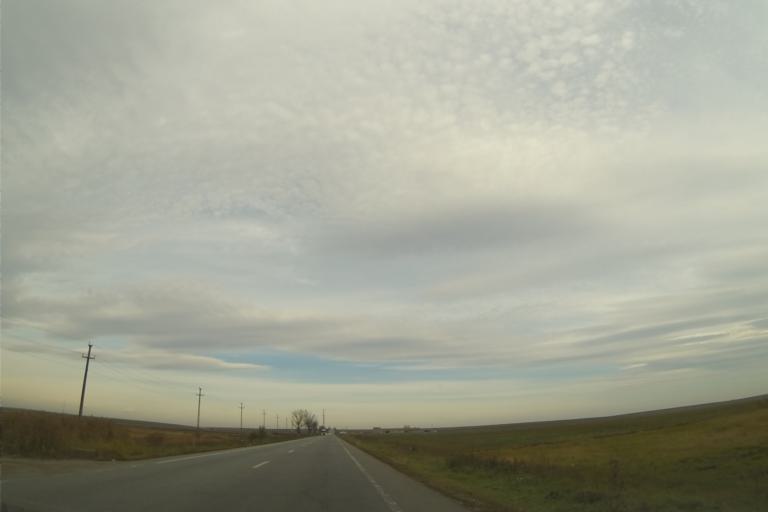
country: RO
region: Olt
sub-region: Comuna Valea Mare
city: Valea Mare
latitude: 44.4661
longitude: 24.4140
